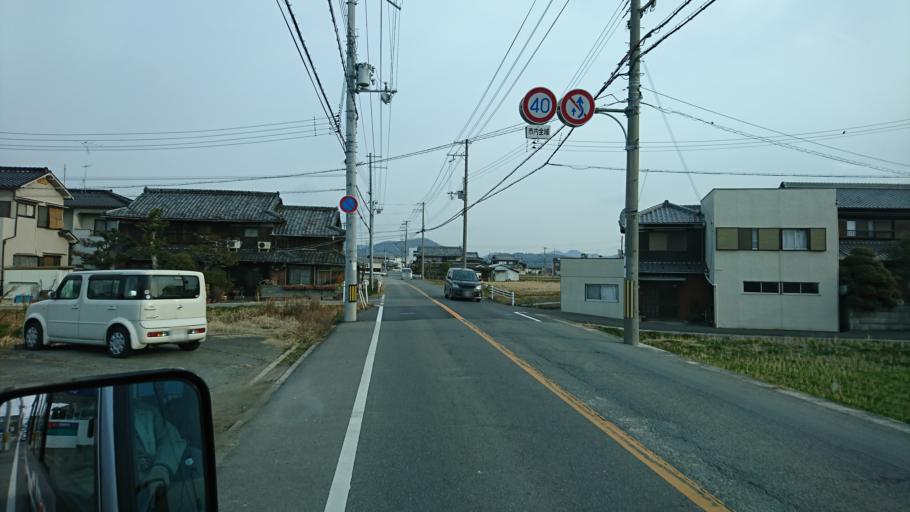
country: JP
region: Hyogo
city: Kakogawacho-honmachi
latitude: 34.8073
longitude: 134.8186
